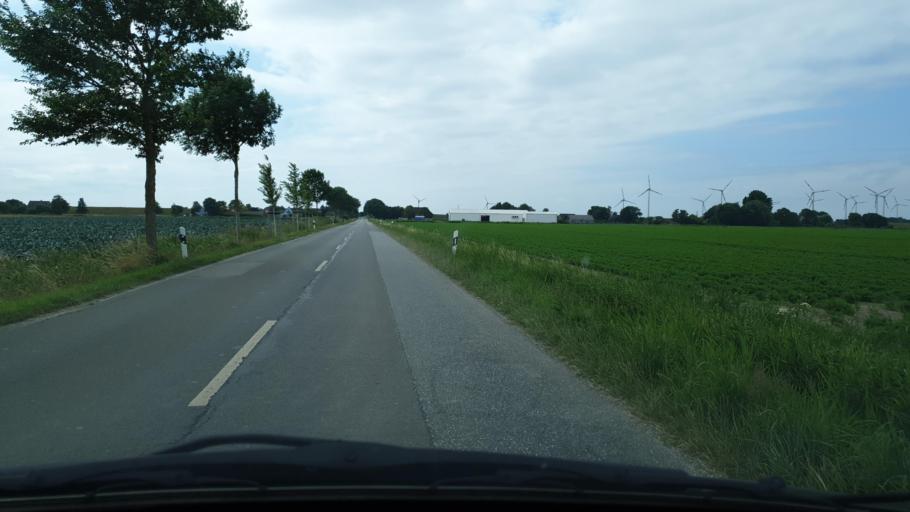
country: DE
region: Schleswig-Holstein
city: Kronprinzenkoog
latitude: 53.9482
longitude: 8.9540
